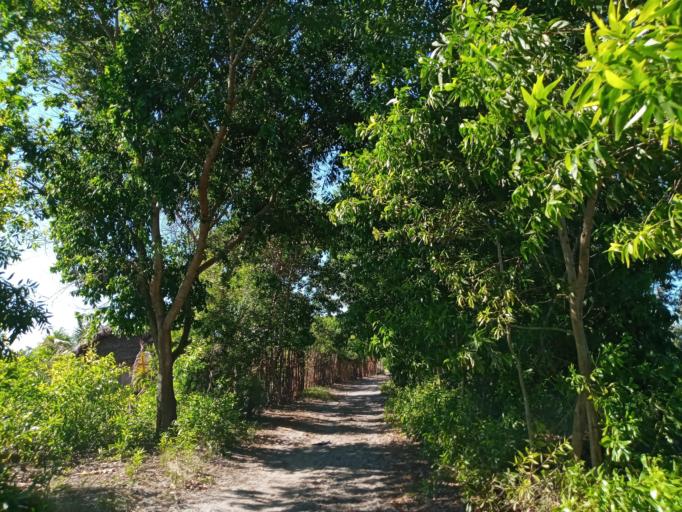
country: MG
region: Anosy
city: Fort Dauphin
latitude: -24.9058
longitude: 47.0983
